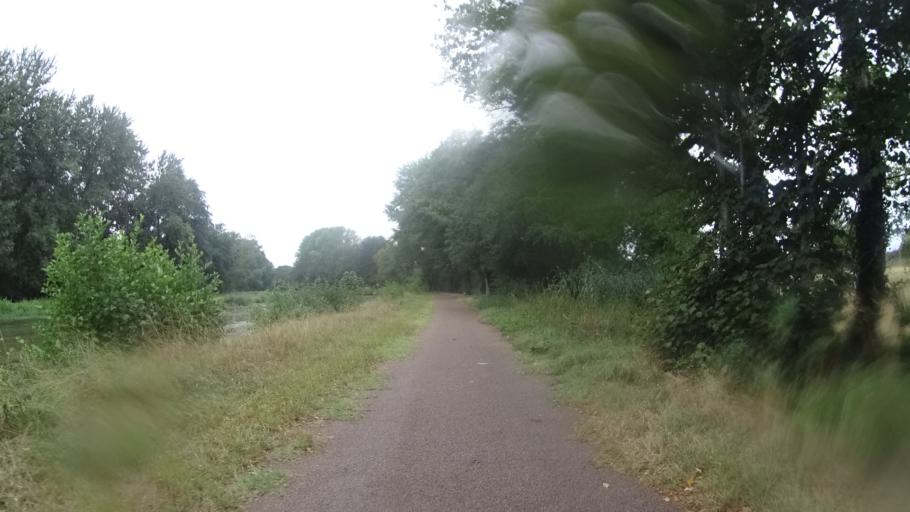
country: FR
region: Bourgogne
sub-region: Departement de la Nievre
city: Decize
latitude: 46.8194
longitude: 3.4480
